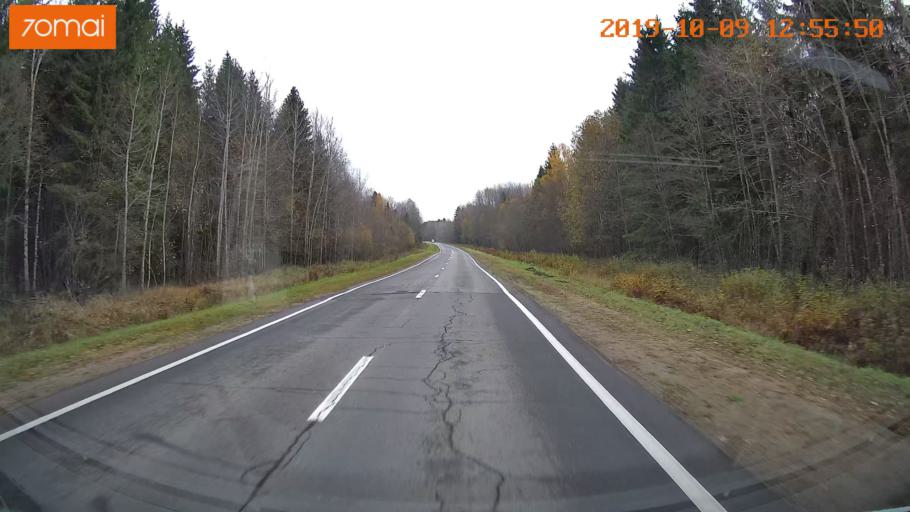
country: RU
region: Jaroslavl
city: Prechistoye
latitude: 58.3973
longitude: 40.4031
